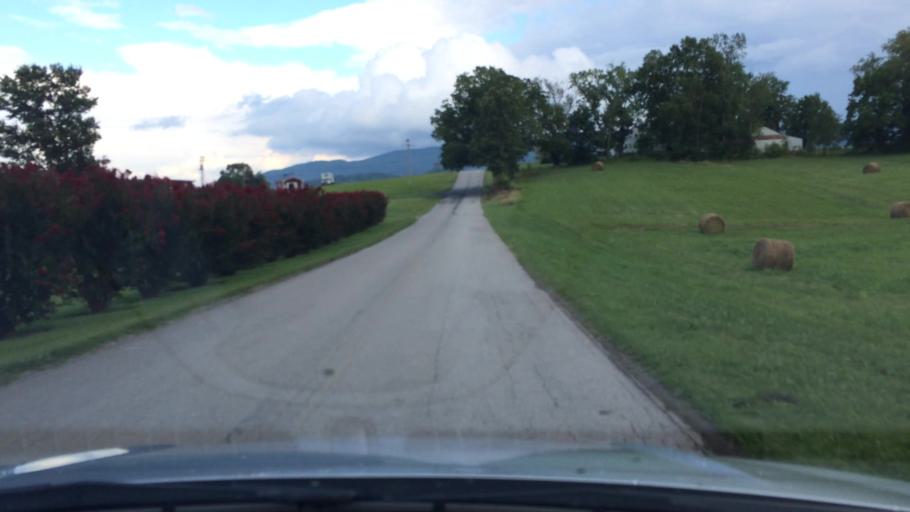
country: US
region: Tennessee
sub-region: Blount County
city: Wildwood
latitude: 35.7566
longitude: -83.8883
